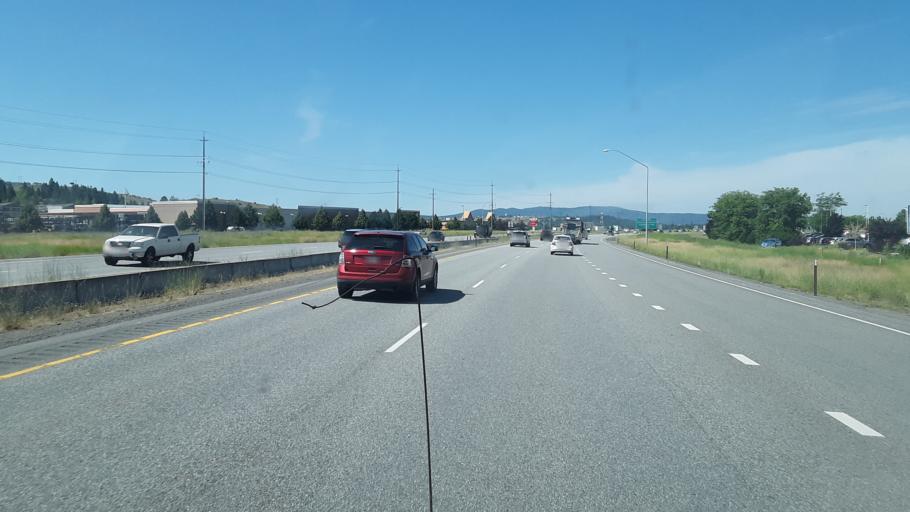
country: US
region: Washington
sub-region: Spokane County
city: Liberty Lake
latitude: 47.6710
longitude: -117.1134
